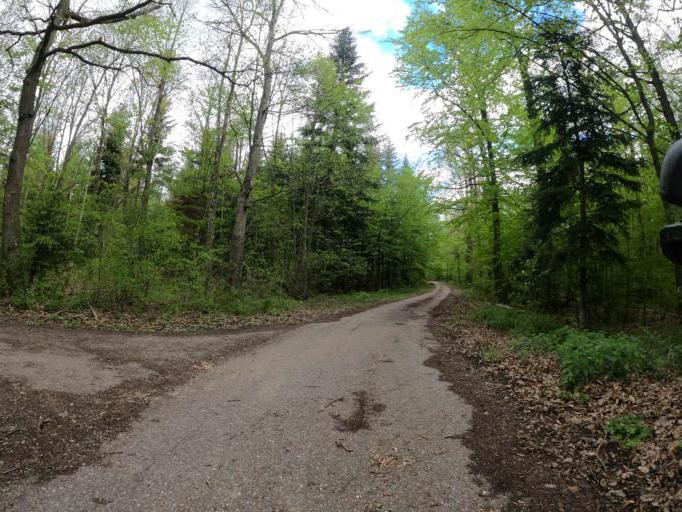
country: DE
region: Baden-Wuerttemberg
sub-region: Regierungsbezirk Stuttgart
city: Nufringen
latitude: 48.6073
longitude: 8.8931
